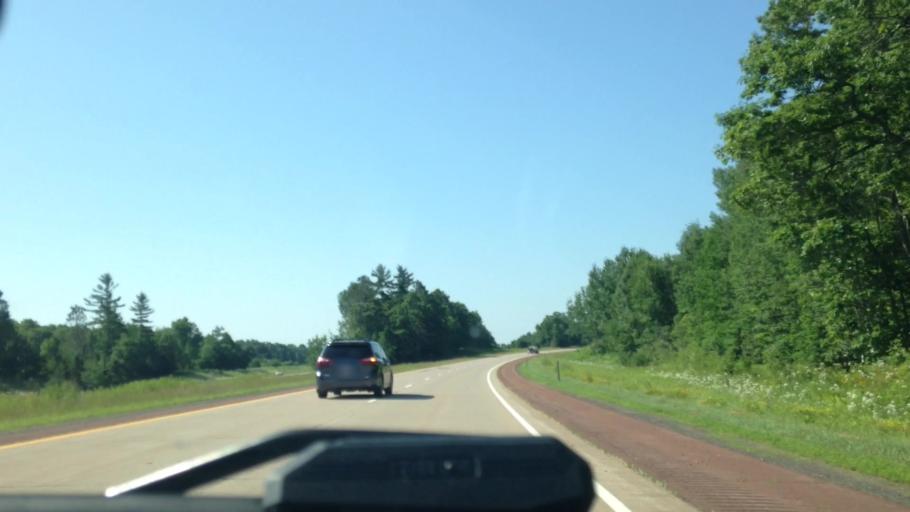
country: US
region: Wisconsin
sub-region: Douglas County
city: Lake Nebagamon
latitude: 46.3917
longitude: -91.8191
